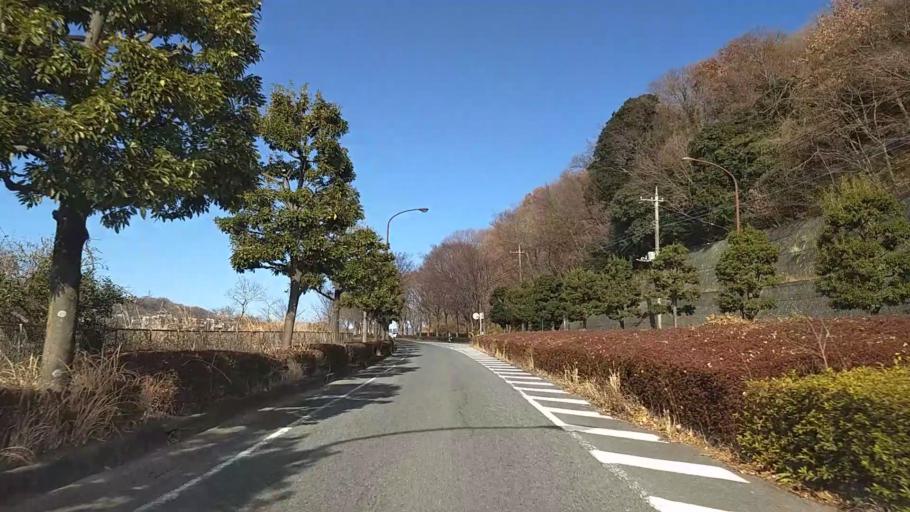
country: JP
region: Kanagawa
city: Atsugi
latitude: 35.4380
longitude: 139.3129
